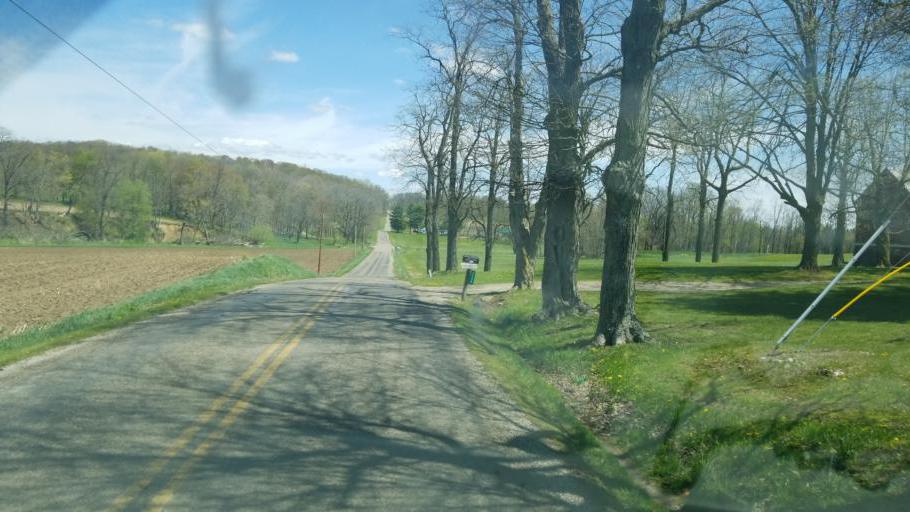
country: US
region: Ohio
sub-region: Richland County
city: Lincoln Heights
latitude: 40.7417
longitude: -82.4295
